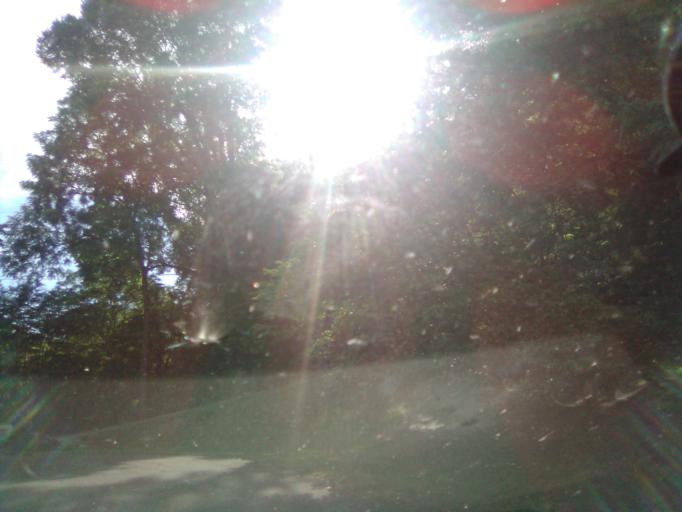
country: US
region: Tennessee
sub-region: Davidson County
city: Belle Meade
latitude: 36.1066
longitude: -86.9084
